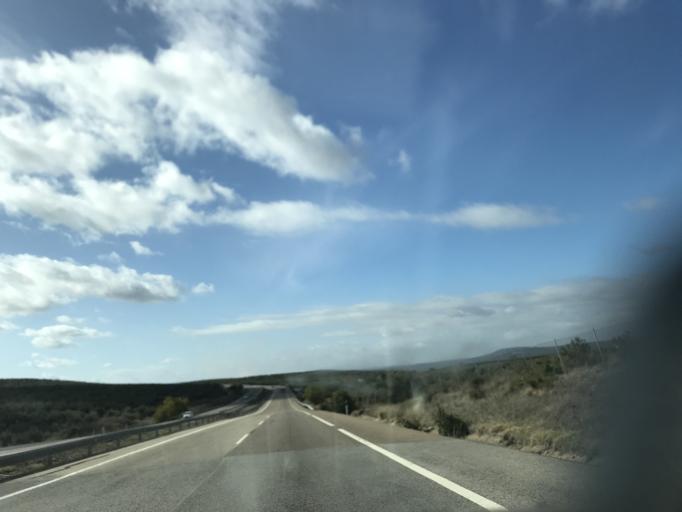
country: ES
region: Andalusia
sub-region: Provincia de Jaen
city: Lopera
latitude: 38.0072
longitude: -4.2242
